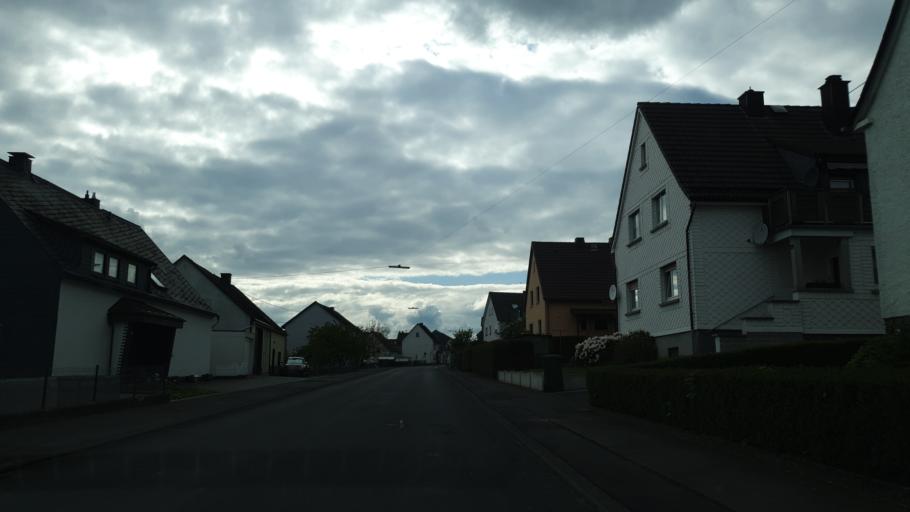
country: DE
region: Rheinland-Pfalz
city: Langenbach bei Marienberg
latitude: 50.6223
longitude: 7.9515
